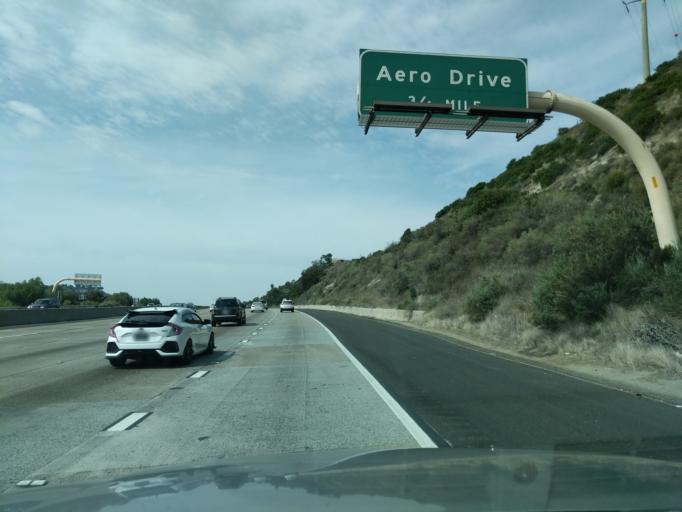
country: US
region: California
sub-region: San Diego County
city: San Diego
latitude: 32.7943
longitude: -117.1118
